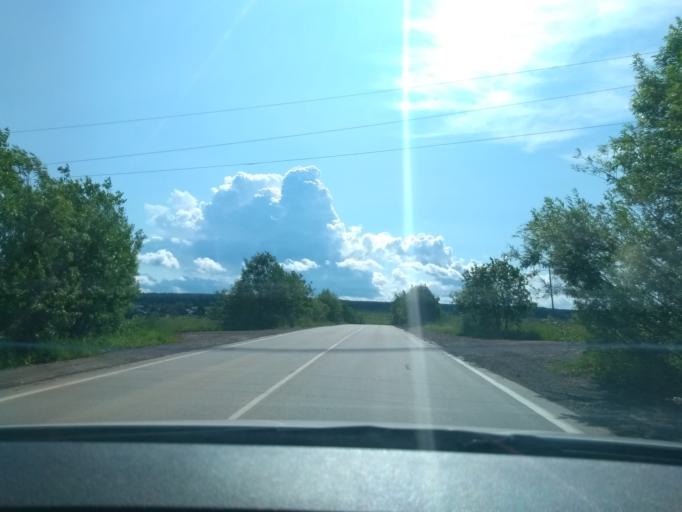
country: RU
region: Perm
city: Bershet'
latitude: 57.8140
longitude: 56.4507
